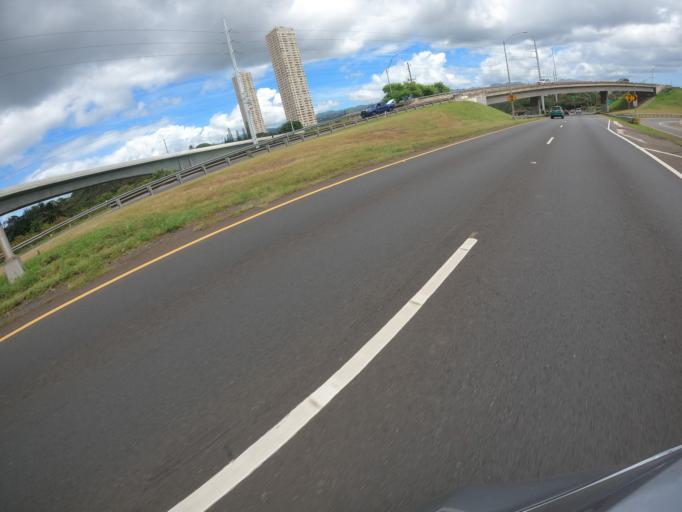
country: US
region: Hawaii
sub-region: Honolulu County
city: Pearl City, Manana
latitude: 21.3964
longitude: -157.9824
